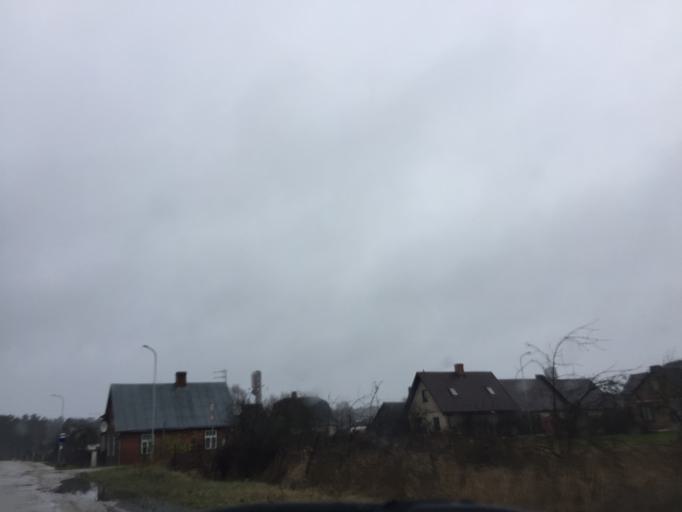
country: LV
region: Jekabpils Rajons
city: Jekabpils
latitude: 56.4894
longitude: 25.8536
